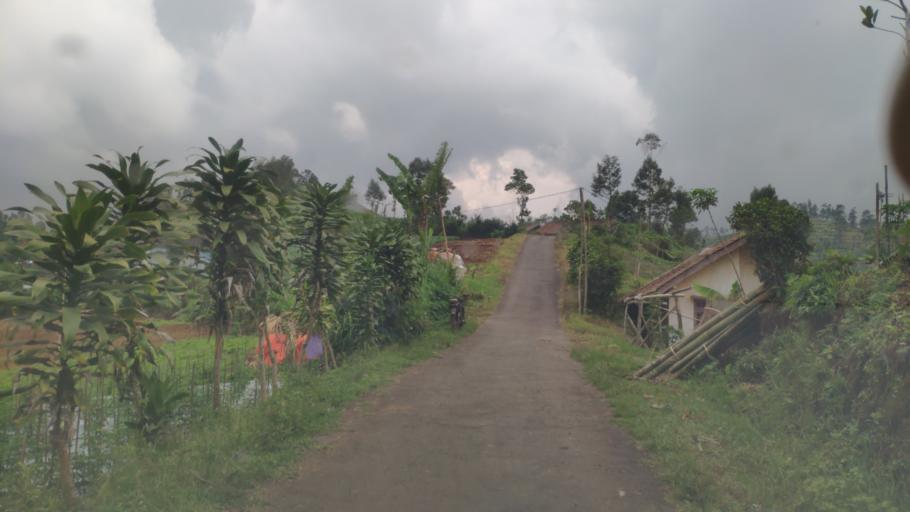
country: ID
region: Central Java
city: Wonosobo
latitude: -7.2319
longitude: 109.7782
